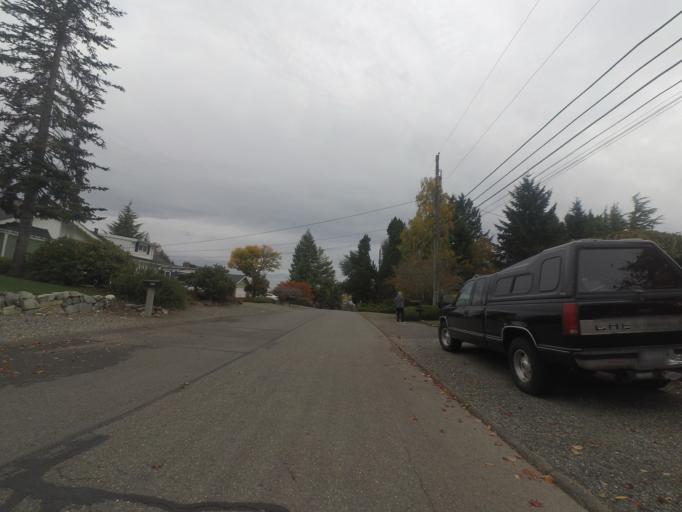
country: US
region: Washington
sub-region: Pierce County
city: University Place
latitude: 47.2222
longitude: -122.5631
